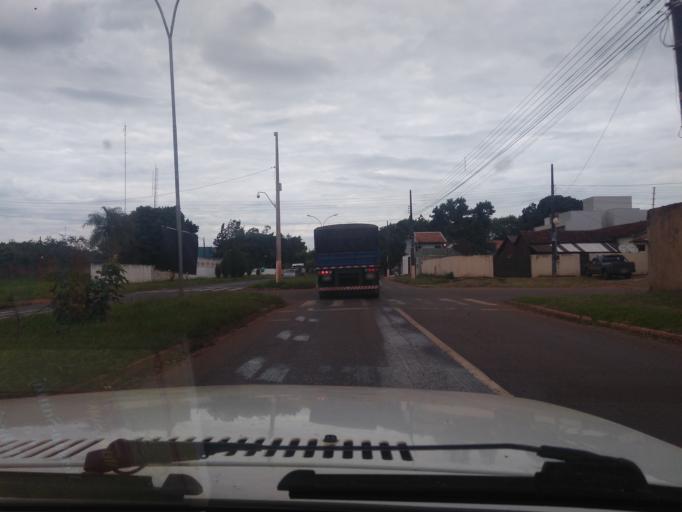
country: BR
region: Mato Grosso do Sul
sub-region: Ponta Pora
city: Ponta Pora
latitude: -22.5223
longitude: -55.7374
